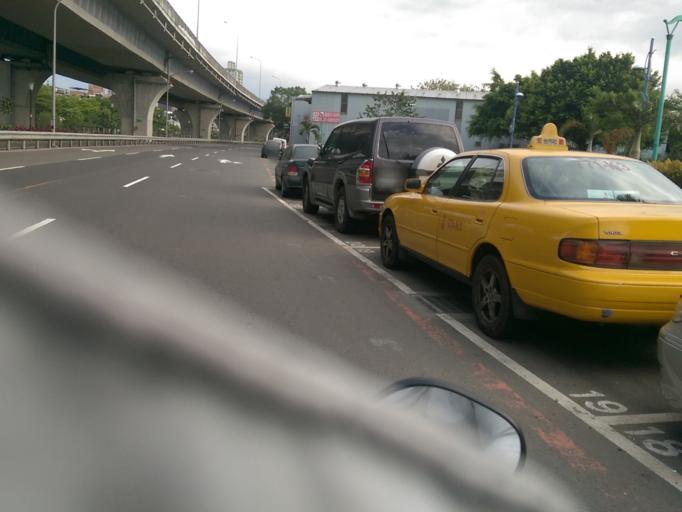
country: TW
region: Taipei
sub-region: Taipei
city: Banqiao
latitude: 25.0143
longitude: 121.4499
